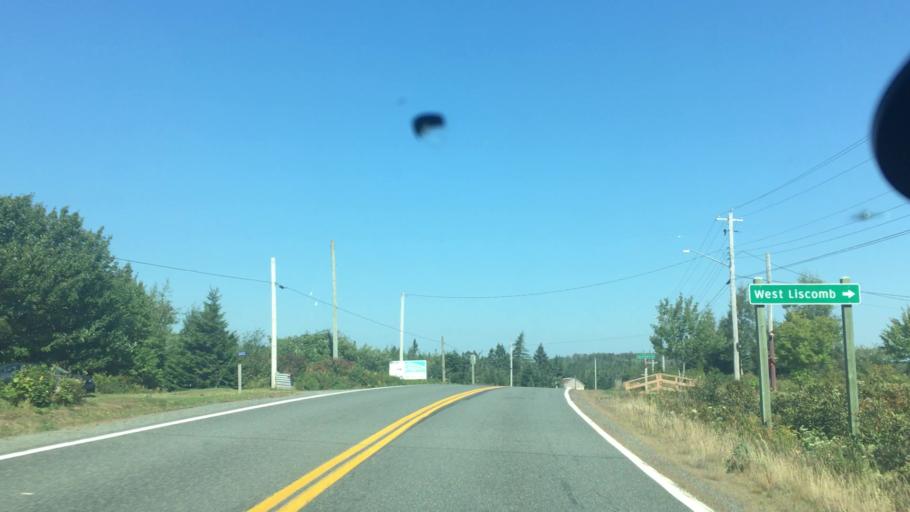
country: CA
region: Nova Scotia
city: Antigonish
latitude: 44.9979
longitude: -62.0998
